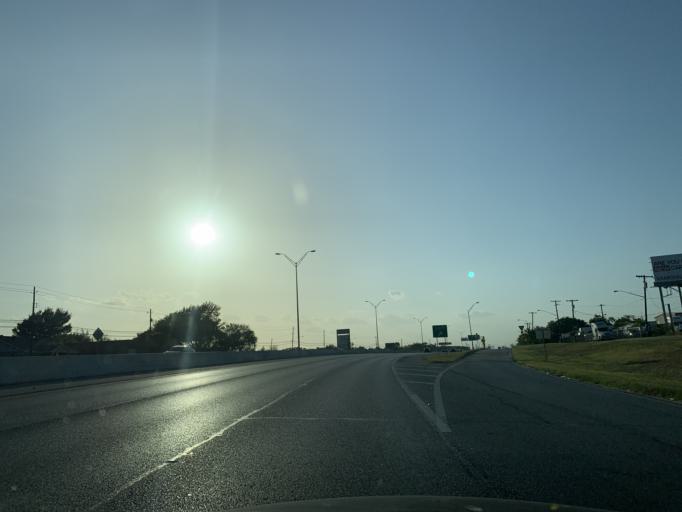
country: US
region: Texas
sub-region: Dallas County
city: Balch Springs
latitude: 32.7055
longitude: -96.6710
